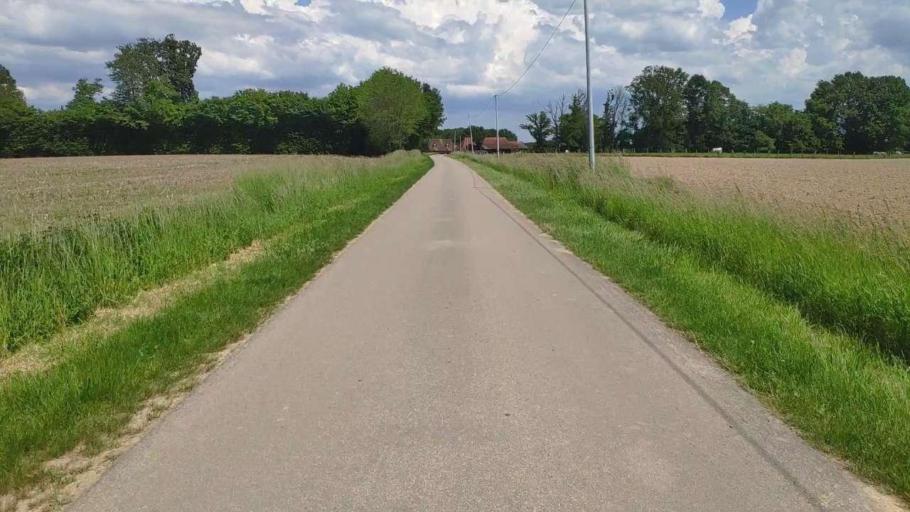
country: FR
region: Franche-Comte
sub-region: Departement du Jura
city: Bletterans
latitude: 46.7886
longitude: 5.4033
